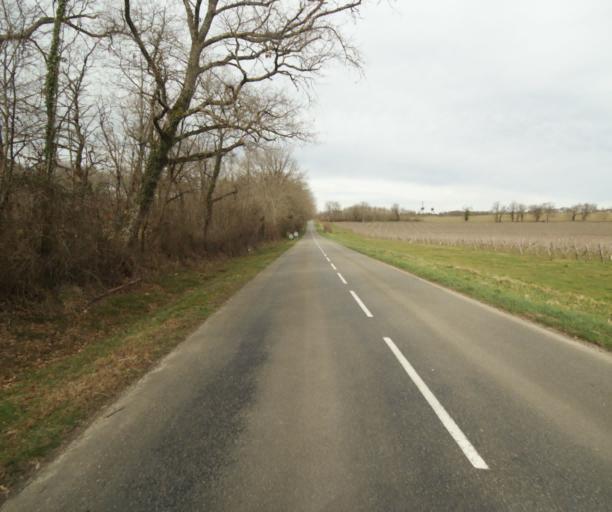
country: FR
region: Aquitaine
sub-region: Departement des Landes
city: Gabarret
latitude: 43.9551
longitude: 0.0086
